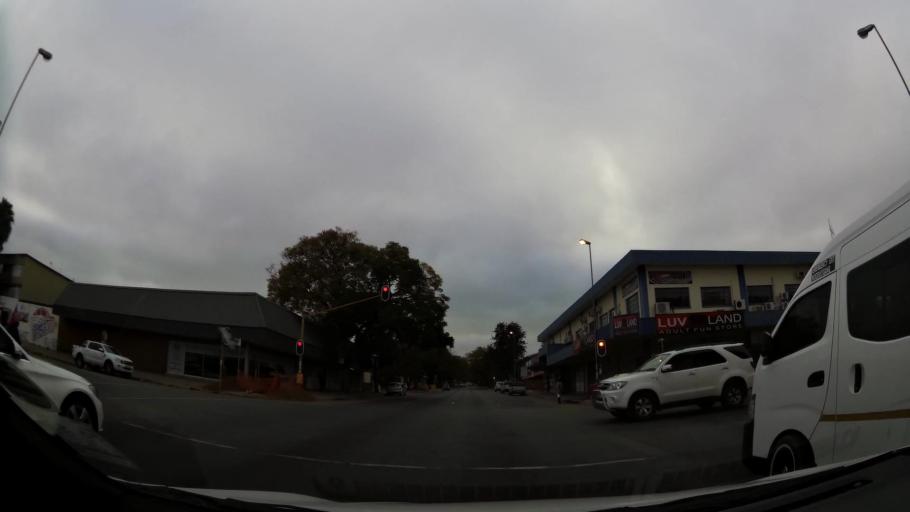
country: ZA
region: Limpopo
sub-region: Capricorn District Municipality
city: Polokwane
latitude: -23.9024
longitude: 29.4519
